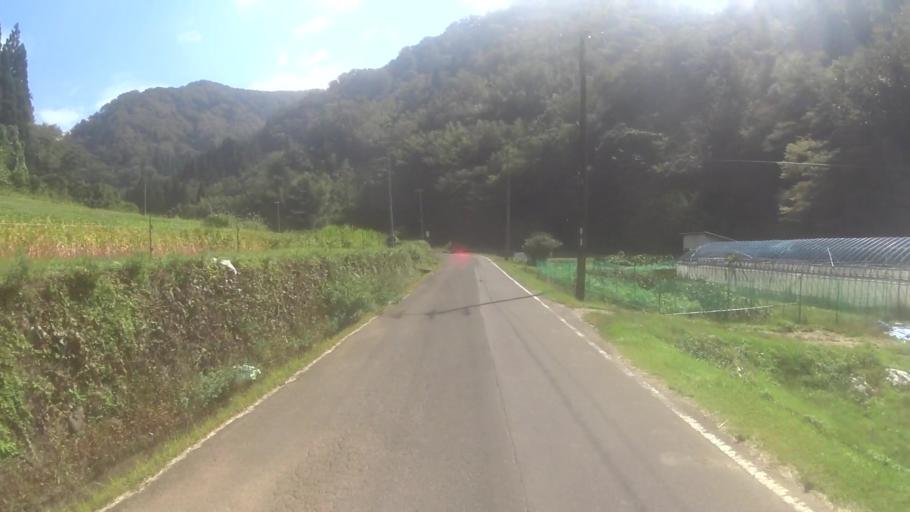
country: JP
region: Kyoto
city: Miyazu
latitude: 35.6811
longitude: 135.1637
